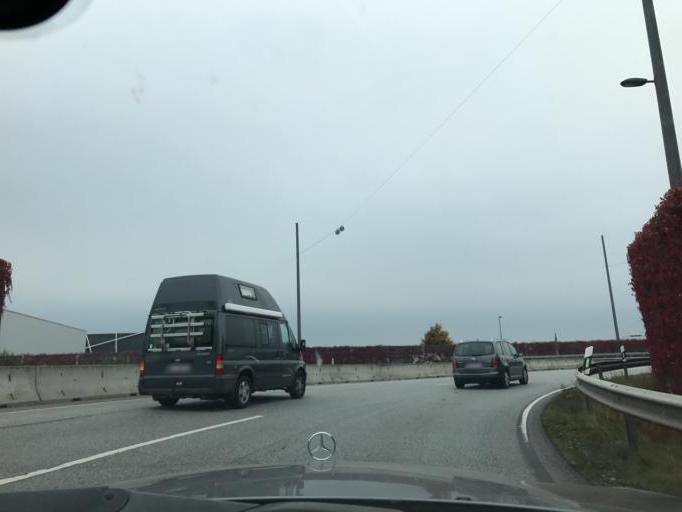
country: DE
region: Bremen
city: Bremen
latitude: 53.0572
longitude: 8.7912
